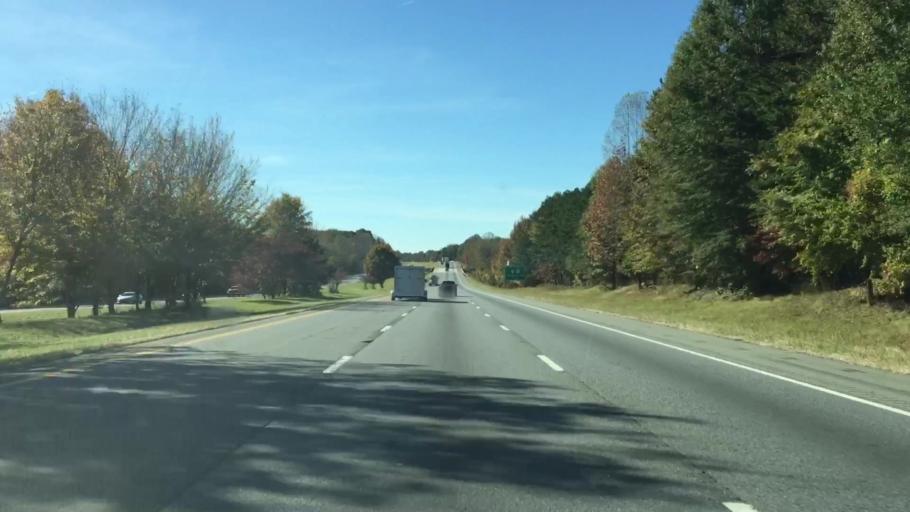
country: US
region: North Carolina
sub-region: Davidson County
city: Lexington
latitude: 35.7769
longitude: -80.2891
